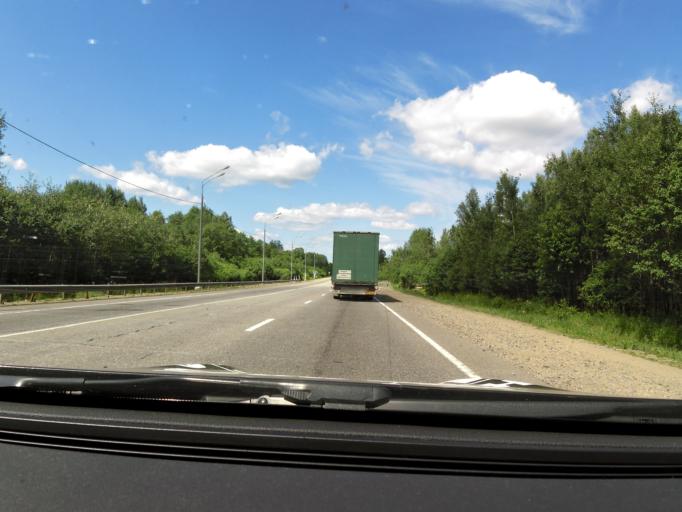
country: RU
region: Tverskaya
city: Kuzhenkino
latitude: 57.7874
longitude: 33.8960
